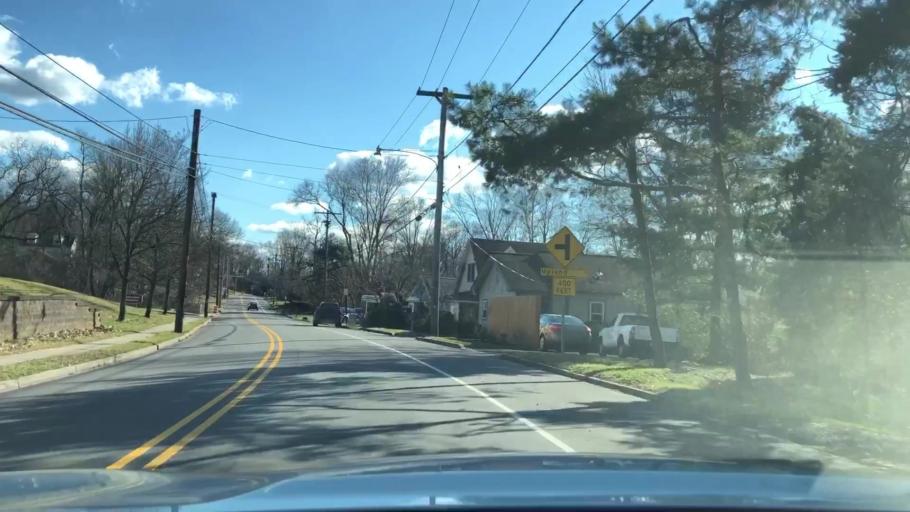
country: US
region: Pennsylvania
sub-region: Montgomery County
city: Pottstown
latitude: 40.2599
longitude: -75.6588
